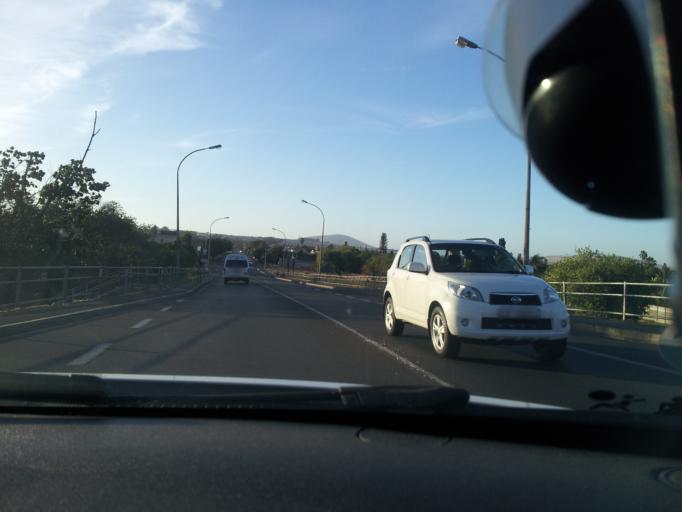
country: ZA
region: Western Cape
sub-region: City of Cape Town
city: Kraaifontein
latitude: -33.8447
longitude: 18.7143
